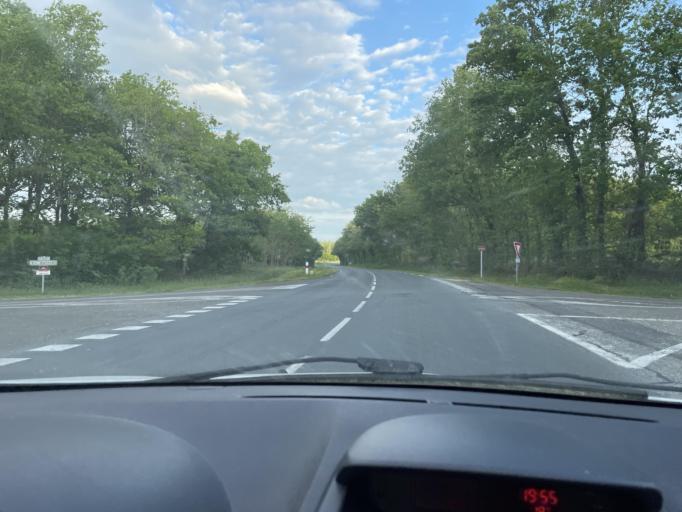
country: FR
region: Aquitaine
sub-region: Departement de la Gironde
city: Grignols
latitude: 44.3572
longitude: 0.0013
